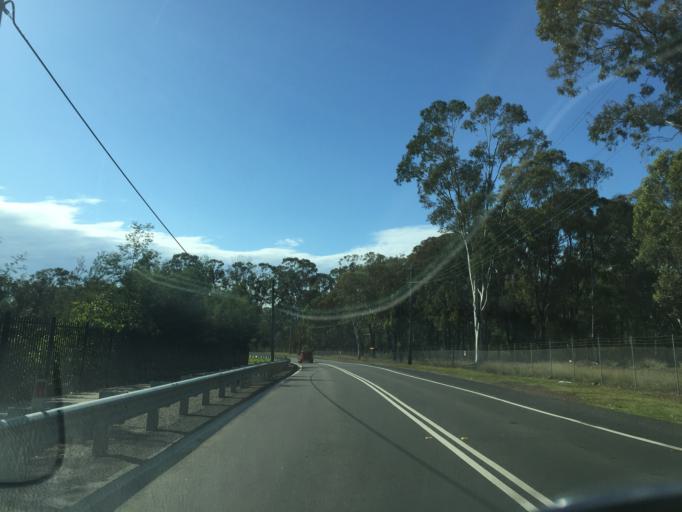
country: AU
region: New South Wales
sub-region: Holroyd
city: Girraween
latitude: -33.8093
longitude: 150.9096
